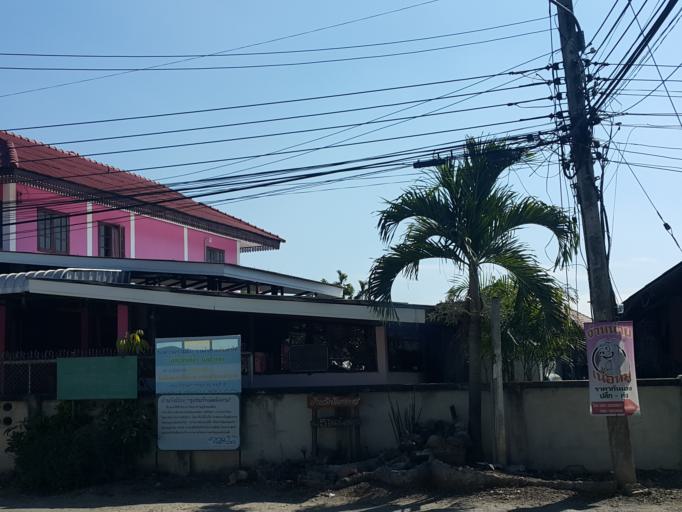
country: TH
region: Chiang Mai
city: San Sai
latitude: 18.8814
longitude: 98.9959
